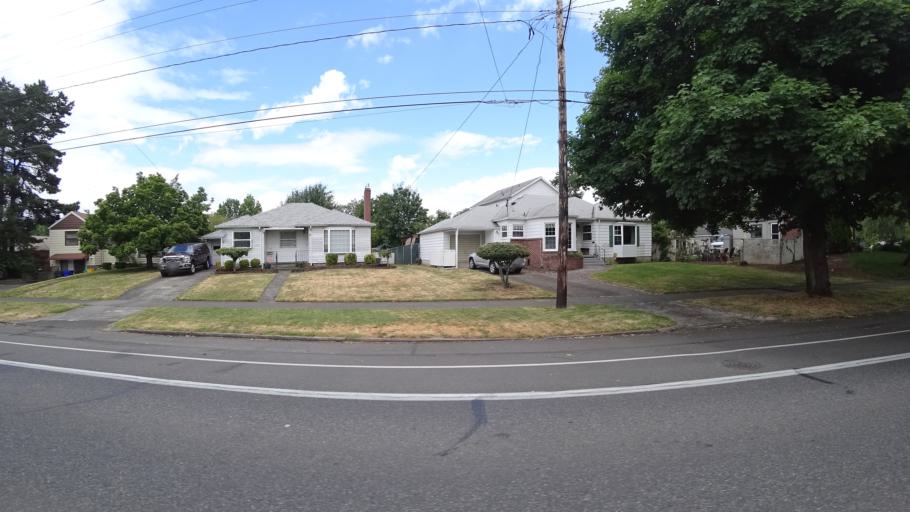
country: US
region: Oregon
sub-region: Washington County
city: West Haven
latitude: 45.5789
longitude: -122.7349
